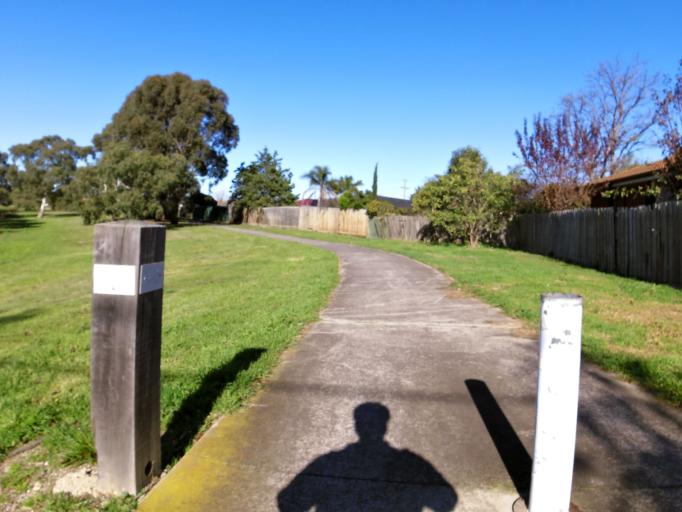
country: AU
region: Victoria
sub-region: Wyndham
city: Tarneit
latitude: -37.8769
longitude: 144.6748
